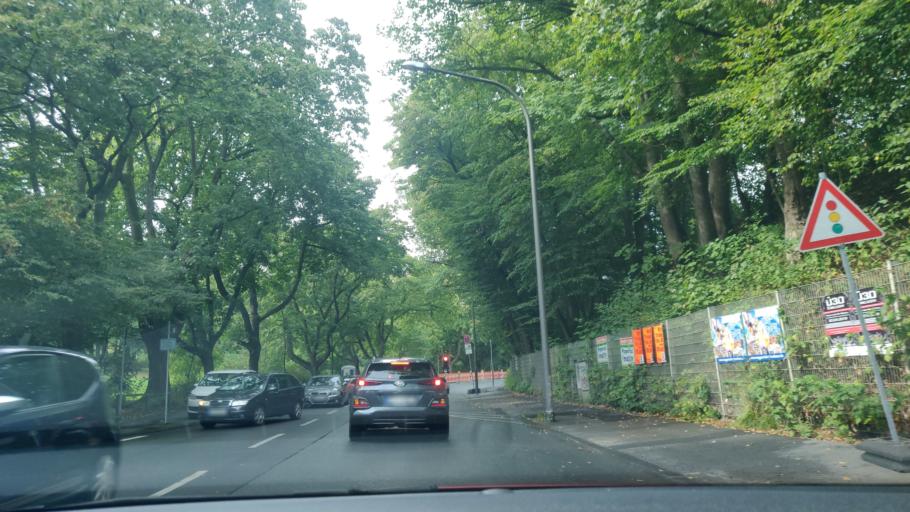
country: DE
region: North Rhine-Westphalia
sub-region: Regierungsbezirk Dusseldorf
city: Wuppertal
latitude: 51.2738
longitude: 7.1231
